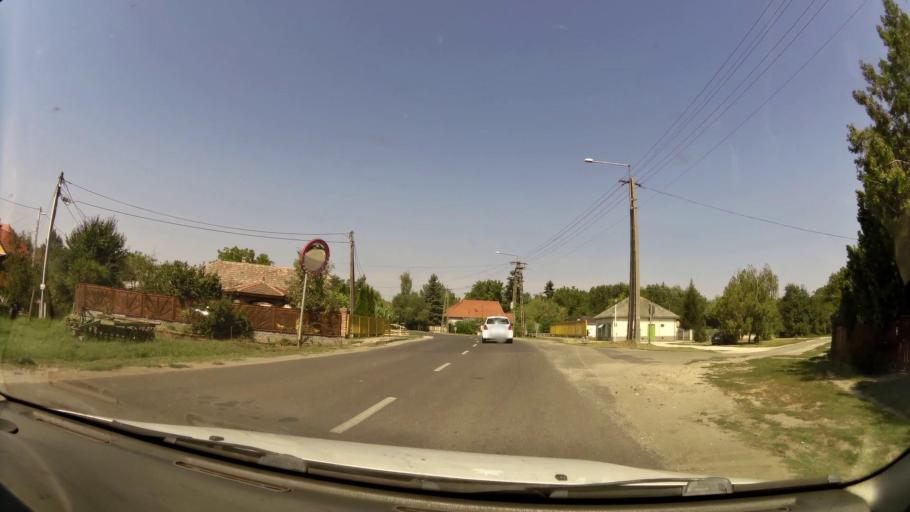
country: HU
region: Pest
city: Tapiobicske
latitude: 47.3588
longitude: 19.6922
